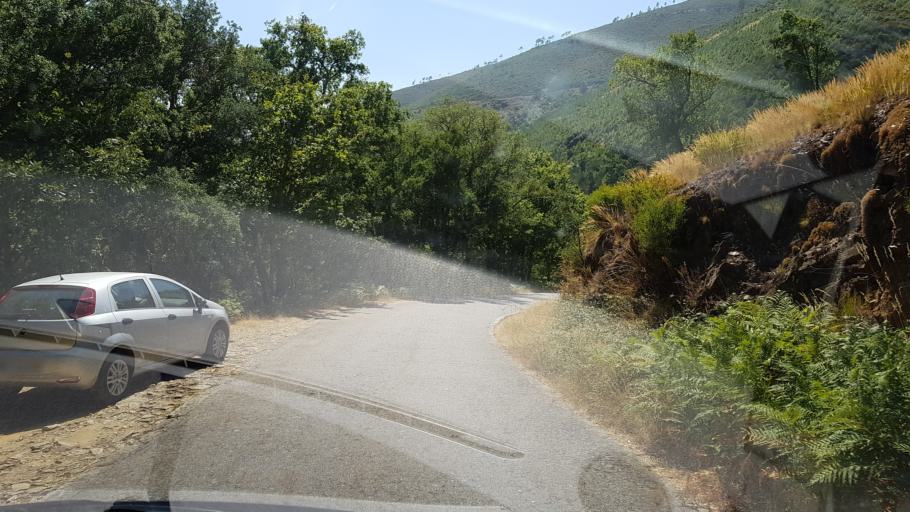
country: PT
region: Vila Real
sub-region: Mondim de Basto
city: Mondim de Basto
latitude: 41.3663
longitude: -7.8919
